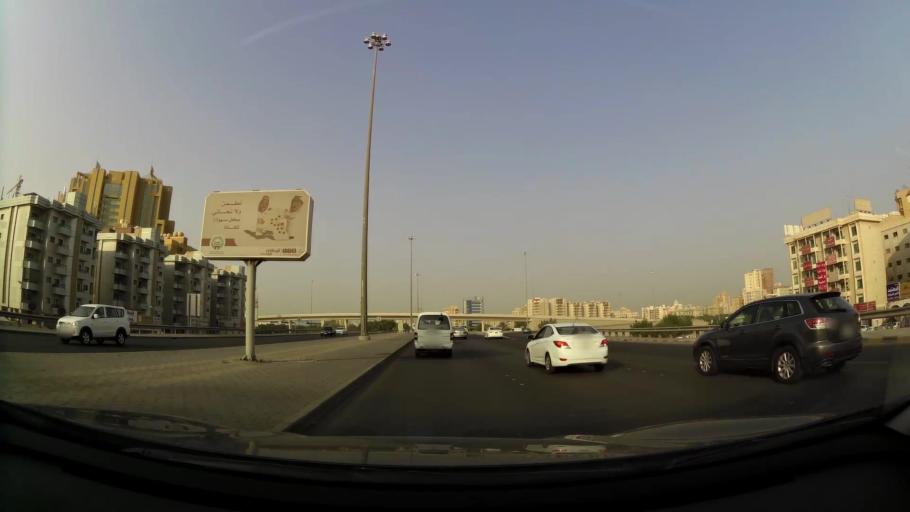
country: KW
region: Muhafazat Hawalli
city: Hawalli
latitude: 29.3316
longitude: 48.0436
